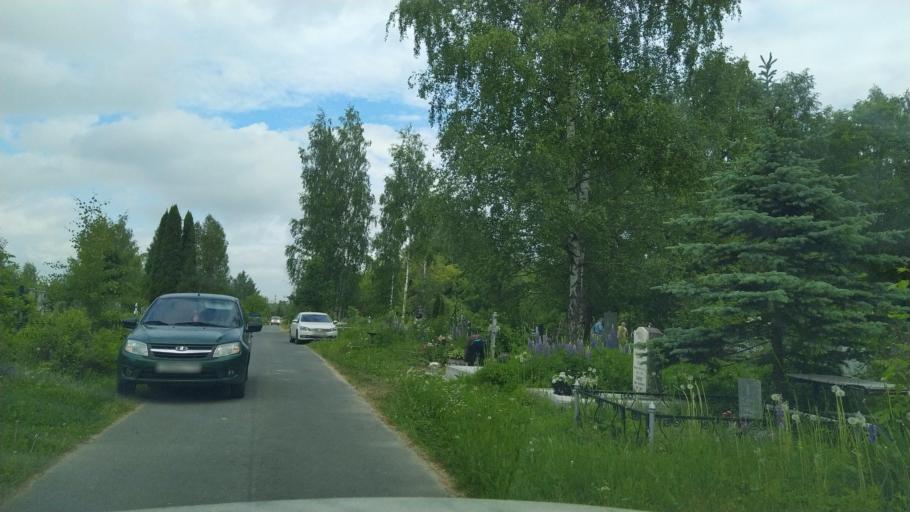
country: RU
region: St.-Petersburg
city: Pushkin
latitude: 59.6926
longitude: 30.3819
